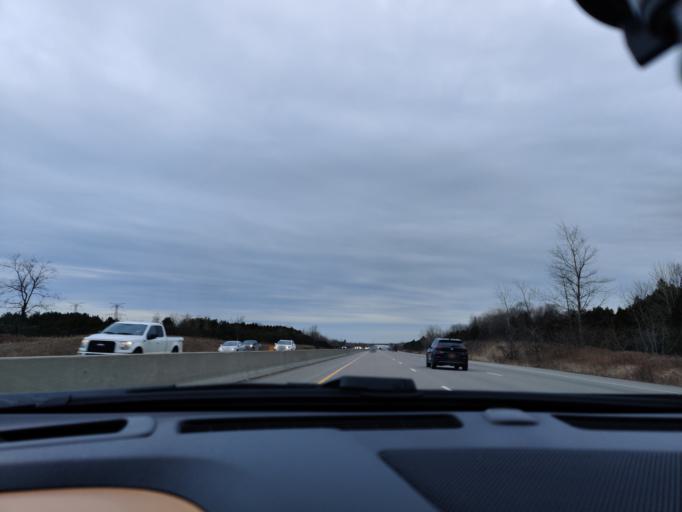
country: CA
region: Ontario
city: Oshawa
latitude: 43.9246
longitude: -78.5184
